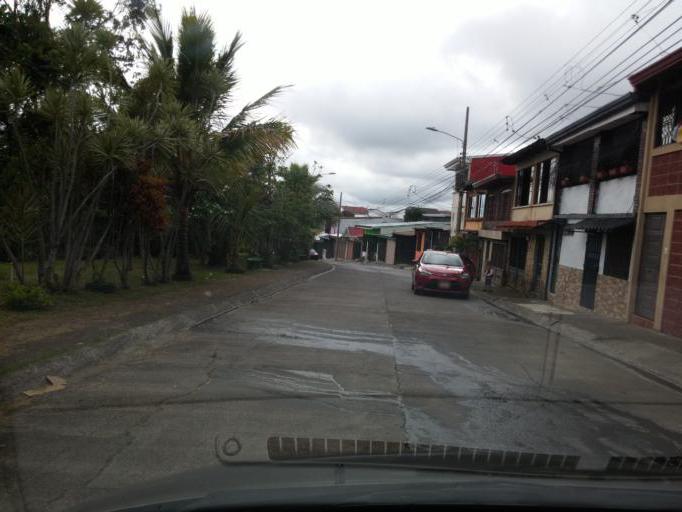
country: CR
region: Heredia
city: Mercedes
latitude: 10.0216
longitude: -84.1290
